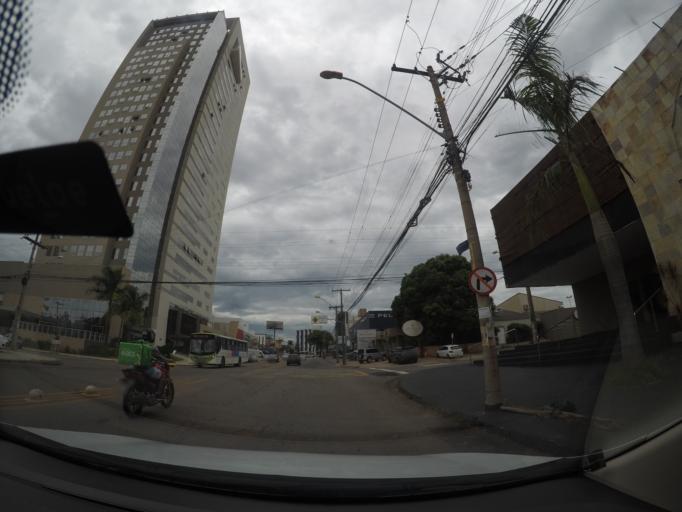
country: BR
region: Goias
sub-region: Goiania
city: Goiania
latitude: -16.7040
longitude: -49.2662
